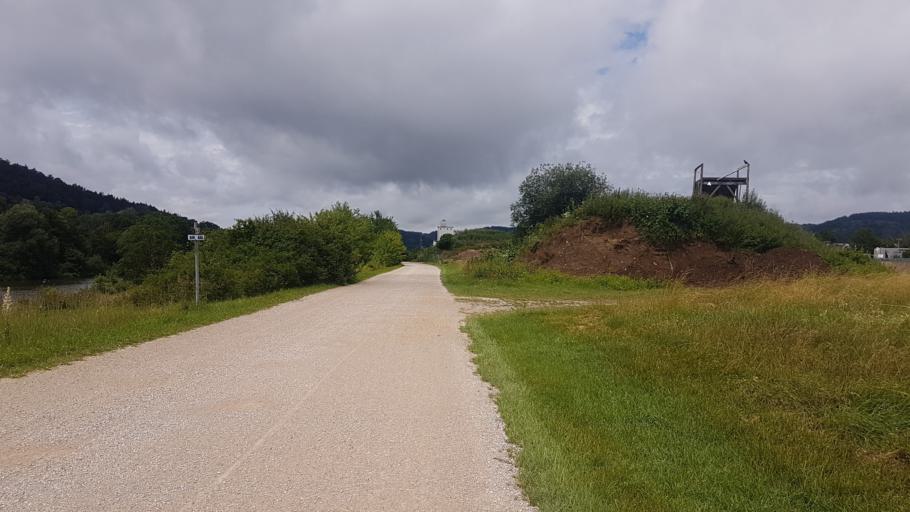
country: DE
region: Bavaria
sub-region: Upper Palatinate
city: Dietfurt
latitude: 49.0198
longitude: 11.5937
